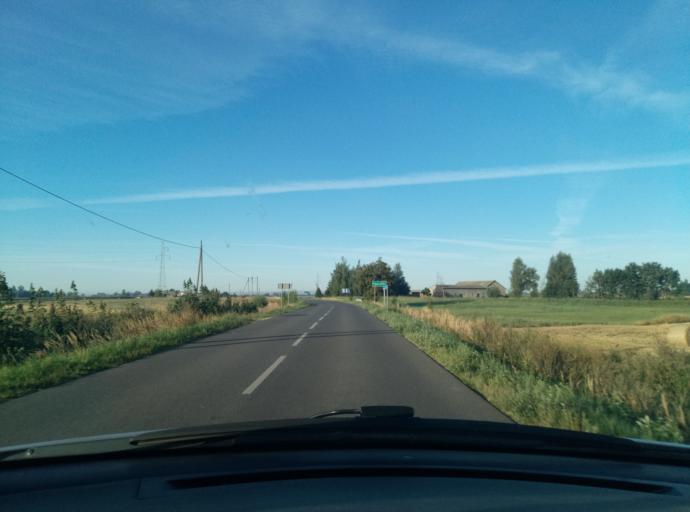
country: PL
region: Kujawsko-Pomorskie
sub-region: Powiat golubsko-dobrzynski
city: Kowalewo Pomorskie
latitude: 53.1831
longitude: 18.9043
